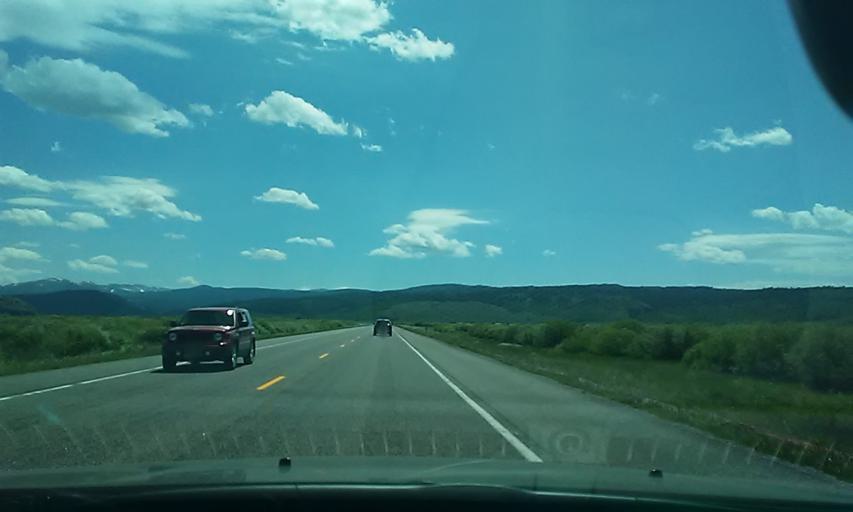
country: US
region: Wyoming
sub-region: Teton County
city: Jackson
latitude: 43.8351
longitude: -110.4304
